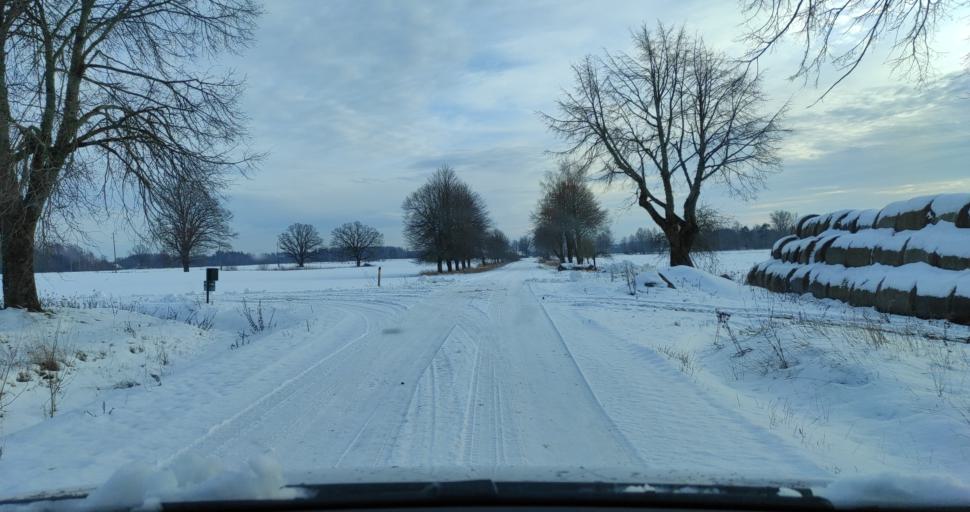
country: LV
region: Kuldigas Rajons
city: Kuldiga
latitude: 56.9463
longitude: 22.0246
